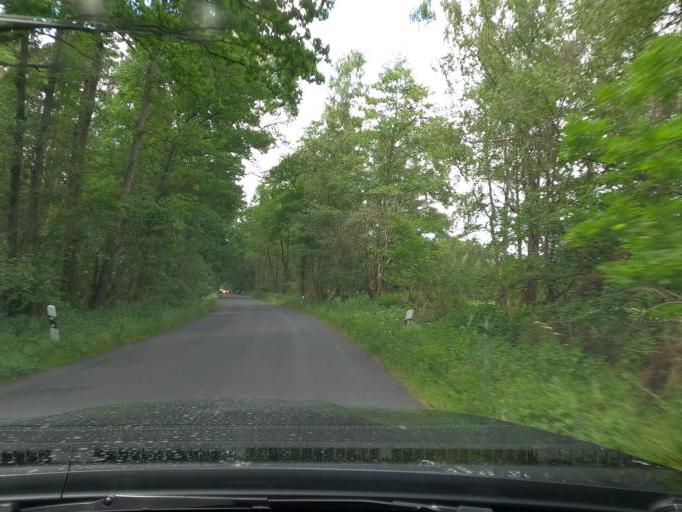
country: DE
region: Lower Saxony
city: Steimbke
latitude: 52.6375
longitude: 9.4663
